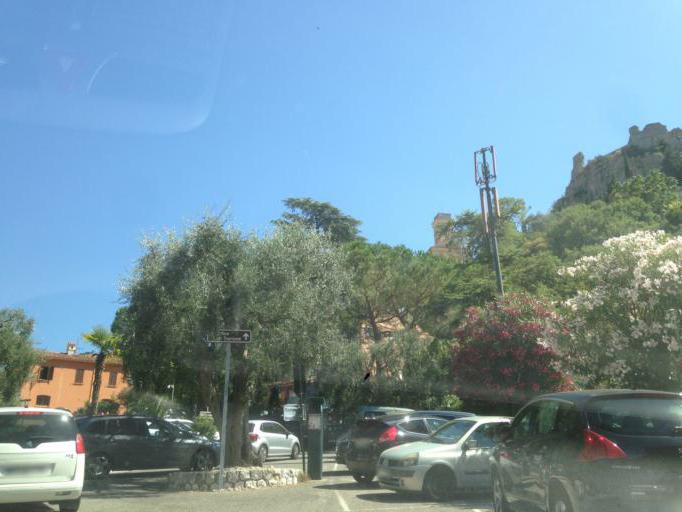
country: FR
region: Provence-Alpes-Cote d'Azur
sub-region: Departement des Alpes-Maritimes
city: Eze
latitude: 43.7297
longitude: 7.3606
